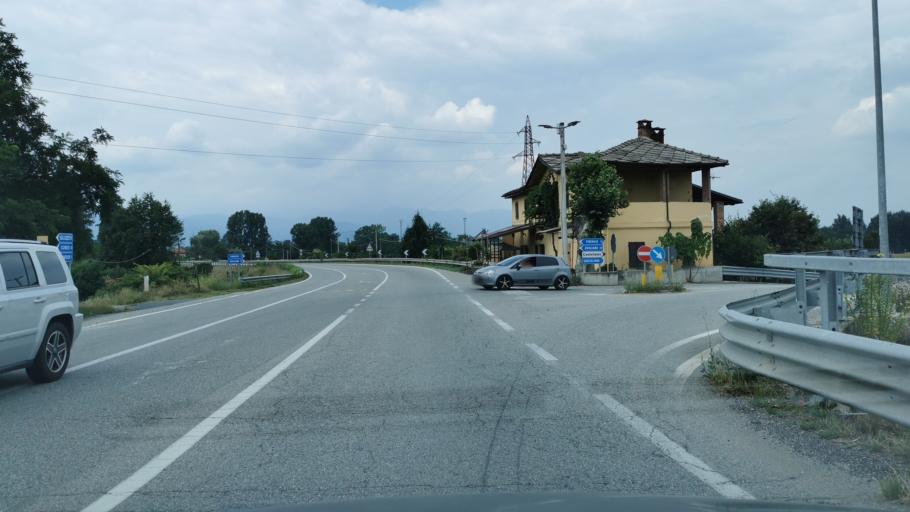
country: IT
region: Piedmont
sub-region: Provincia di Torino
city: Garzigliana
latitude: 44.8294
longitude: 7.3678
